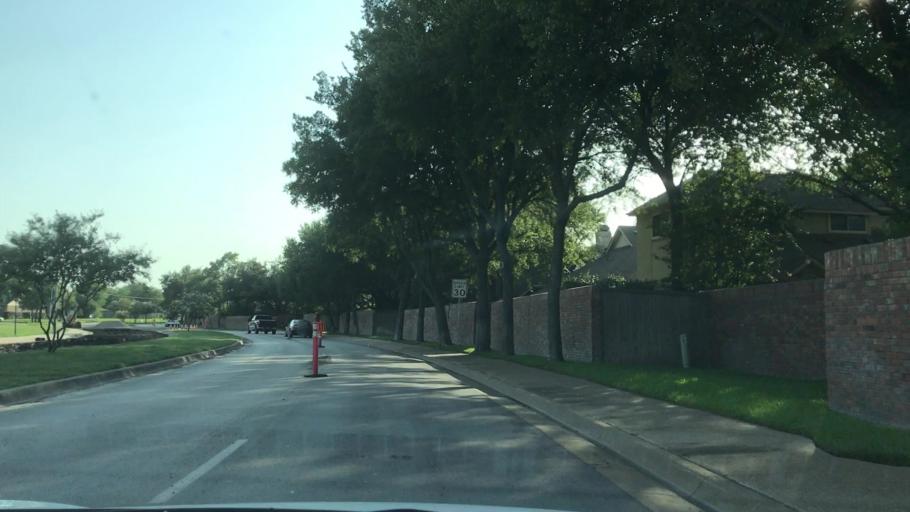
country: US
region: Texas
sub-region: Tarrant County
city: Euless
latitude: 32.8461
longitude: -97.0769
